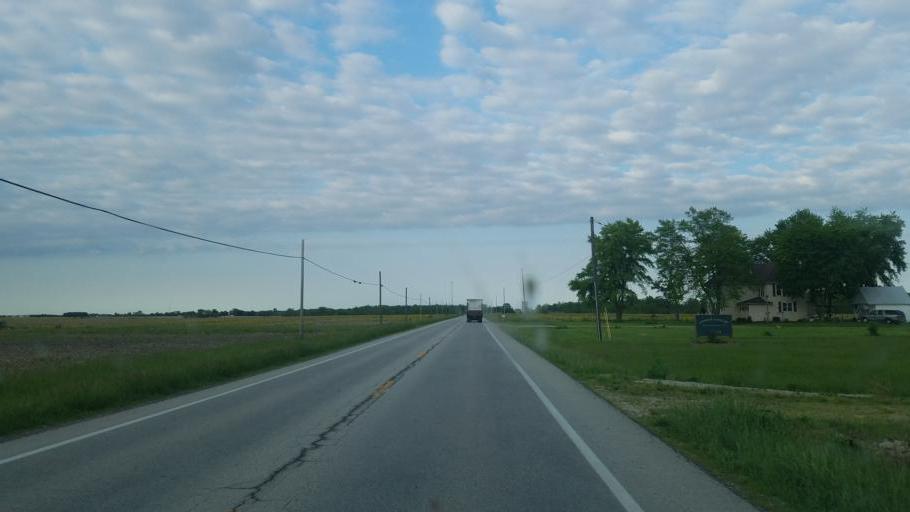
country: US
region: Ohio
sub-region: Madison County
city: Mount Sterling
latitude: 39.7037
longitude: -83.2799
